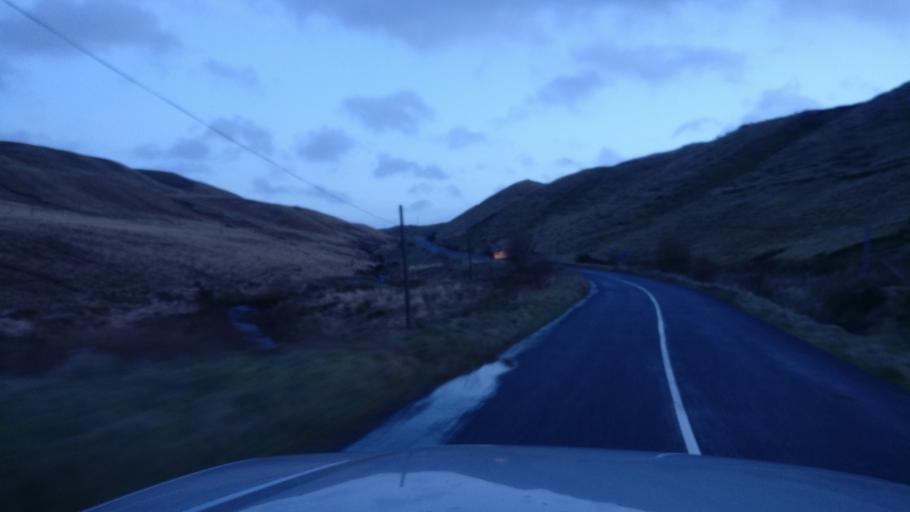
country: IE
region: Connaught
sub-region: Maigh Eo
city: Westport
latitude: 53.5906
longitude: -9.6889
